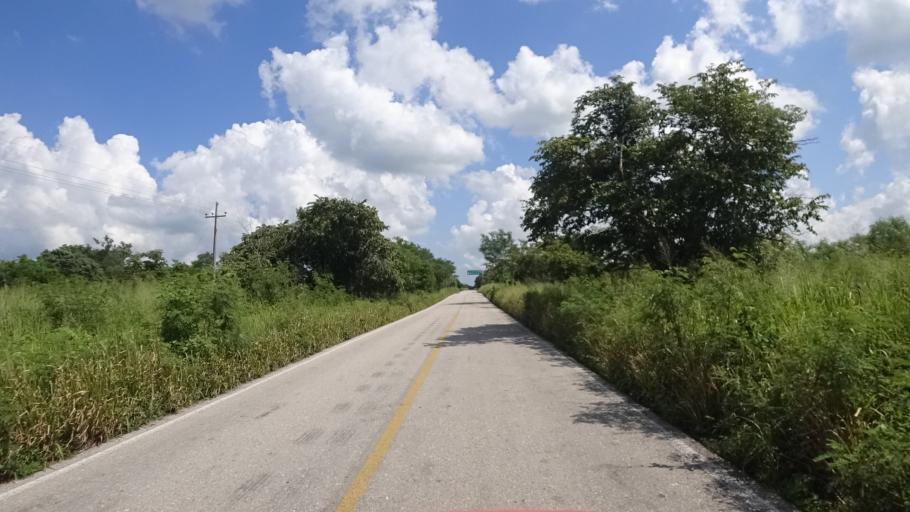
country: MX
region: Yucatan
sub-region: Panaba
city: Loche
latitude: 21.4436
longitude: -88.1391
